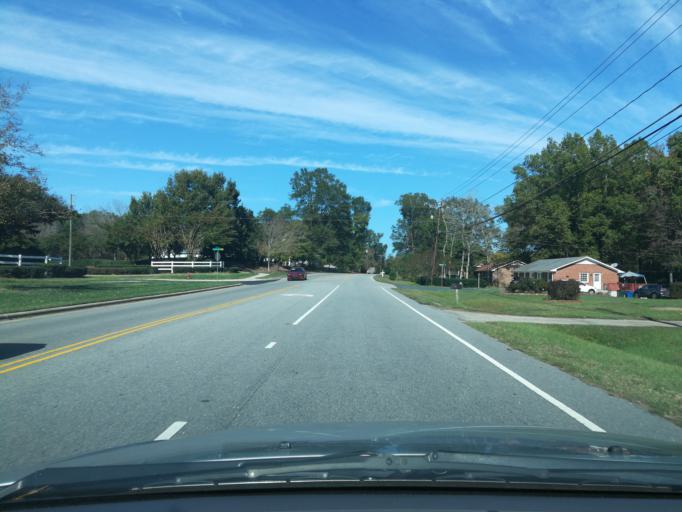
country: US
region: North Carolina
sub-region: Durham County
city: Durham
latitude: 35.9667
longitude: -78.9764
